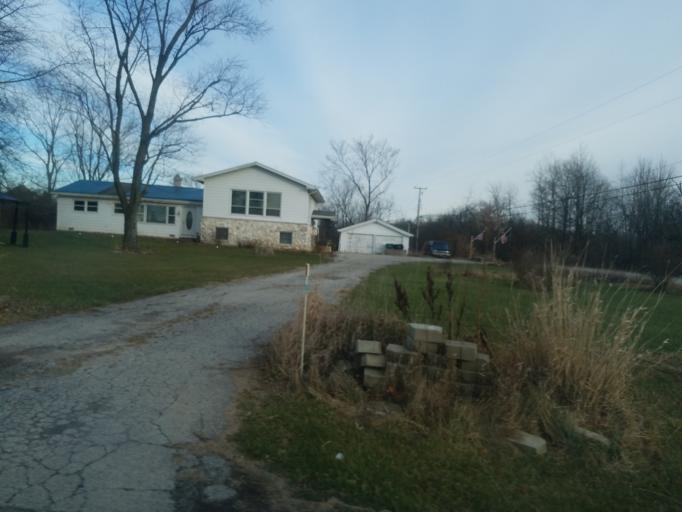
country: US
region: Illinois
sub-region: Will County
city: Homer Glen
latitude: 41.5852
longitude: -87.9488
